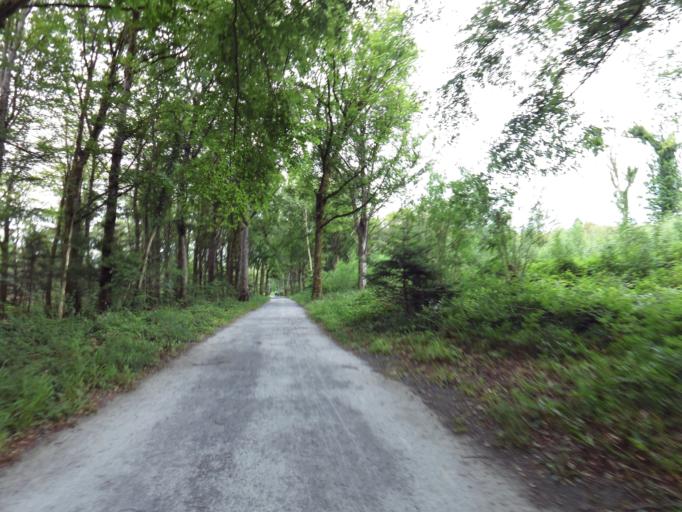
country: IE
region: Connaught
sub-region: County Galway
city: Gort
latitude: 53.0886
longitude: -8.8449
